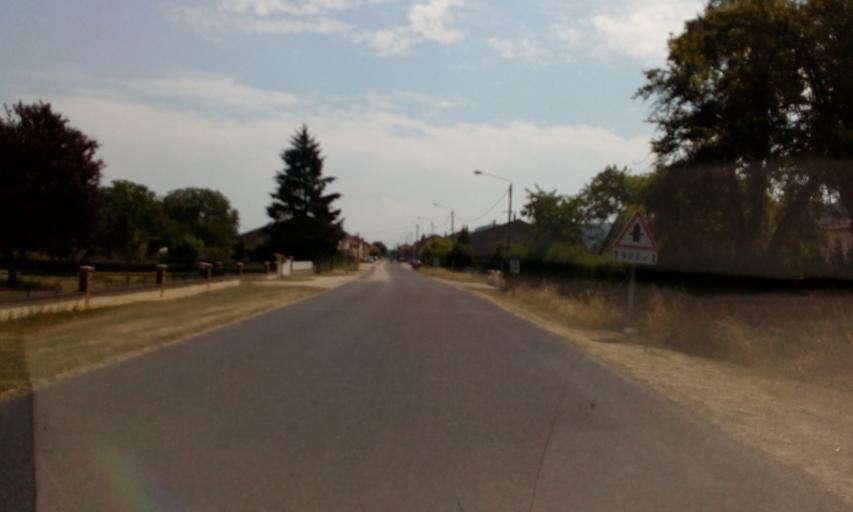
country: FR
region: Lorraine
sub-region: Departement de la Meuse
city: Vigneulles-les-Hattonchatel
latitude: 49.0414
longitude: 5.6542
